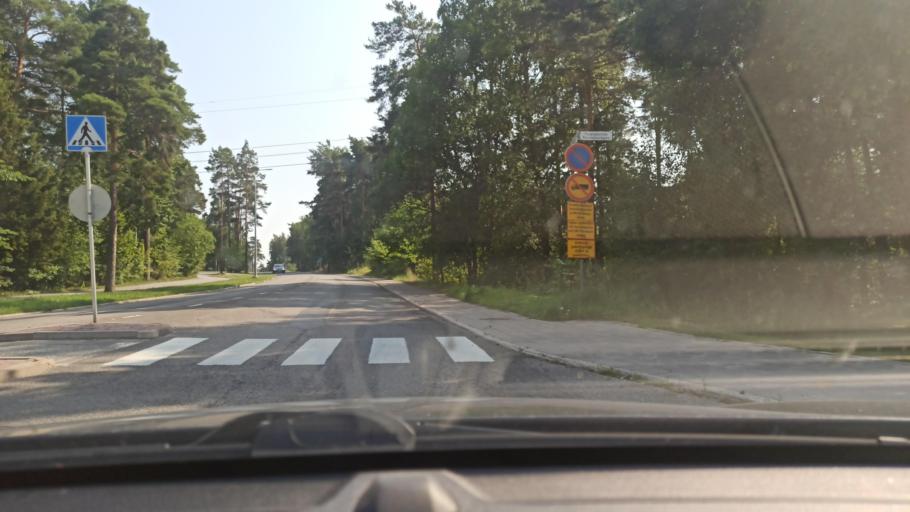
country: FI
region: Varsinais-Suomi
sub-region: Turku
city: Raisio
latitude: 60.4644
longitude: 22.2162
